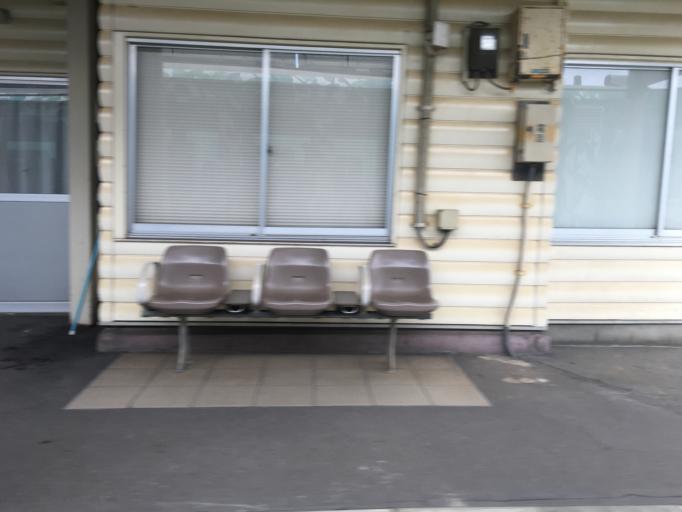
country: JP
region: Aomori
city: Shimokizukuri
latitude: 40.7755
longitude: 140.2207
